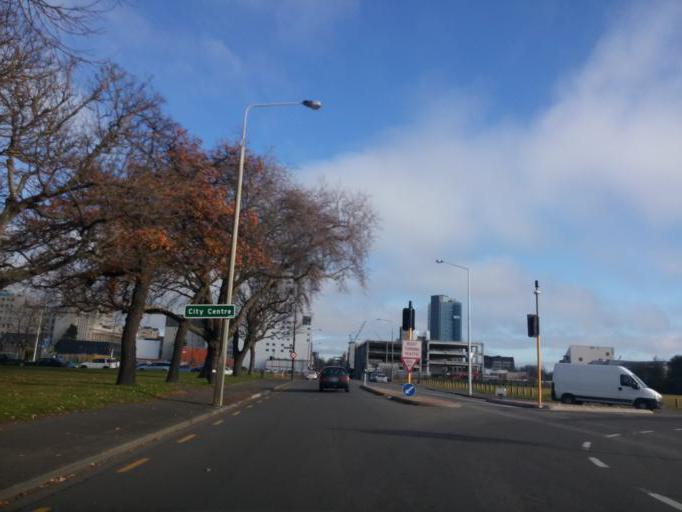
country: NZ
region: Canterbury
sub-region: Christchurch City
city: Christchurch
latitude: -43.5299
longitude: 172.6431
